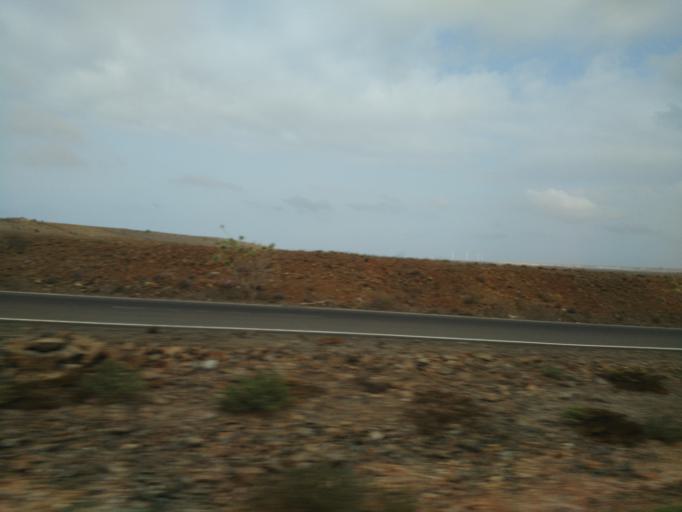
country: CV
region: Sal
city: Espargos
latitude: 16.7143
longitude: -22.9395
